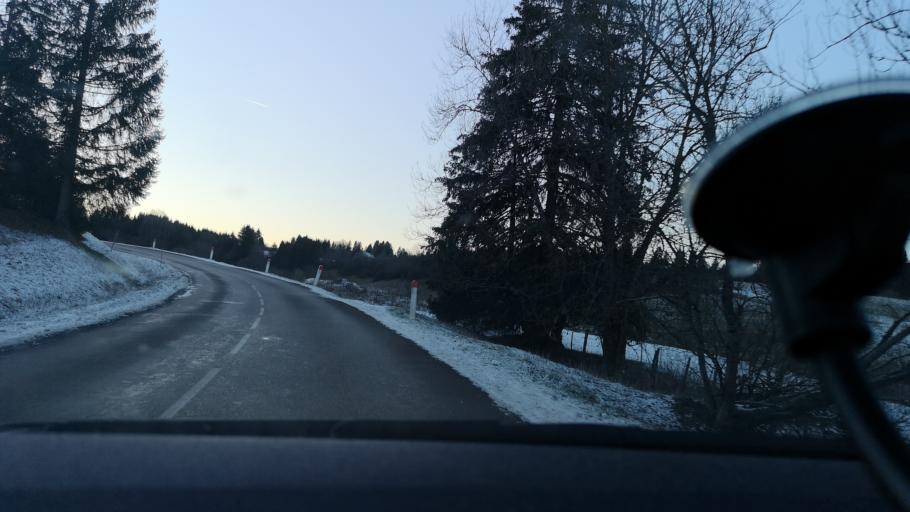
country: FR
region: Franche-Comte
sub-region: Departement du Doubs
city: Pontarlier
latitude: 46.8511
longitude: 6.3270
